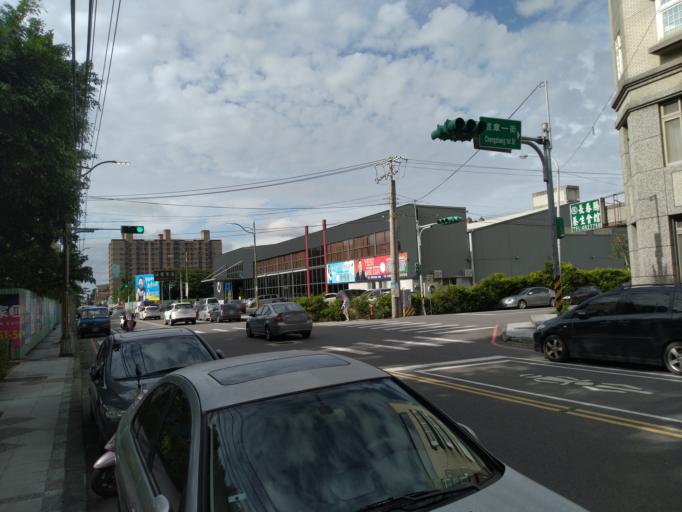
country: TW
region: Taiwan
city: Taoyuan City
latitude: 24.9748
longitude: 121.2533
